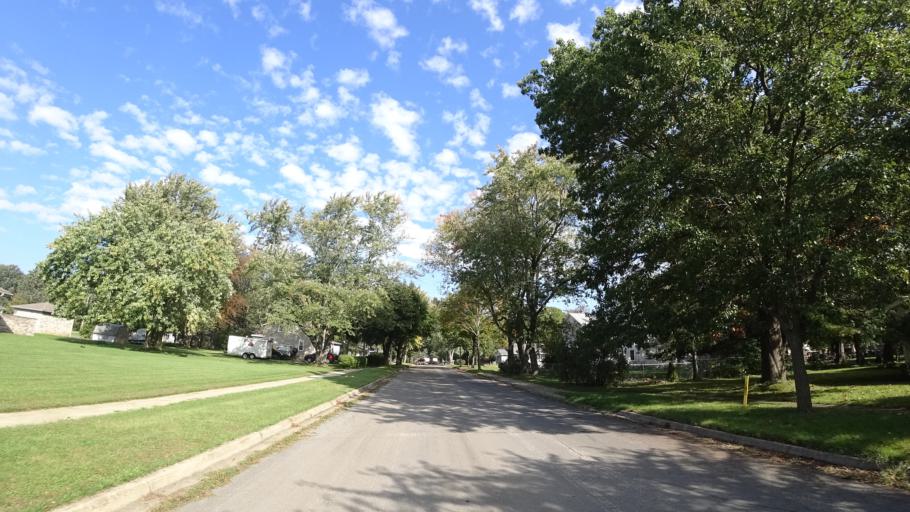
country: US
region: Michigan
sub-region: Saint Joseph County
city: Three Rivers
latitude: 41.9383
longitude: -85.6411
